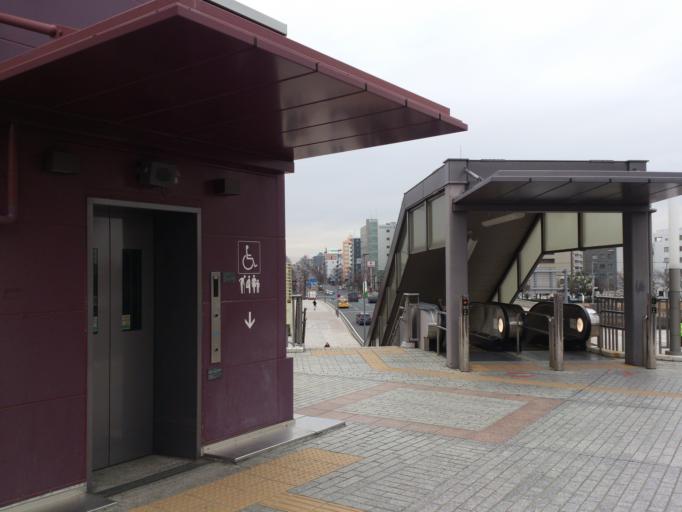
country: JP
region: Ibaraki
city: Mito-shi
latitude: 36.3691
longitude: 140.4761
